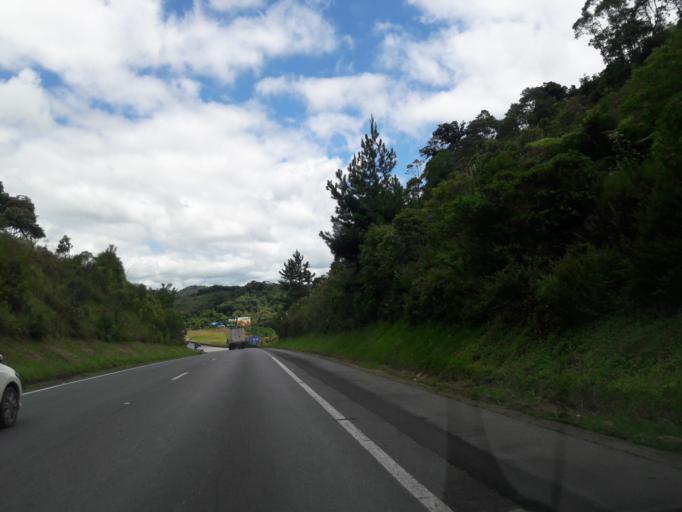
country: BR
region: Parana
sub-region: Antonina
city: Antonina
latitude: -25.1069
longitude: -48.7844
